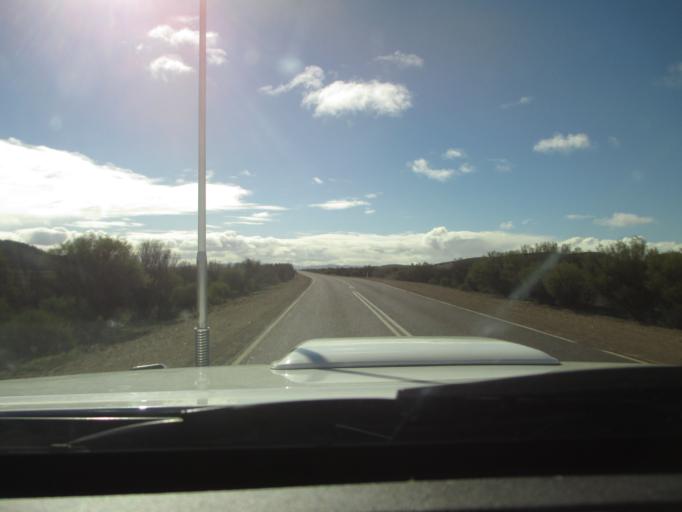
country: AU
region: South Australia
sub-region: Flinders Ranges
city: Quorn
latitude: -31.9343
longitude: 138.4127
